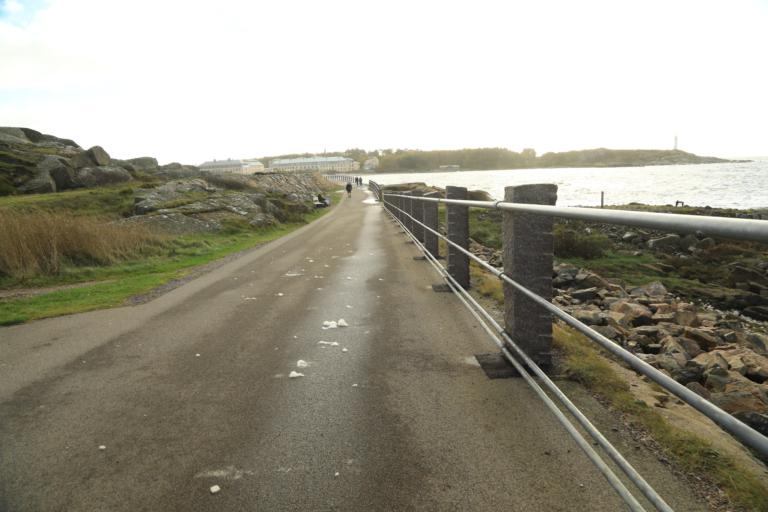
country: SE
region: Halland
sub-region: Varbergs Kommun
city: Varberg
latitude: 57.0930
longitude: 12.2402
